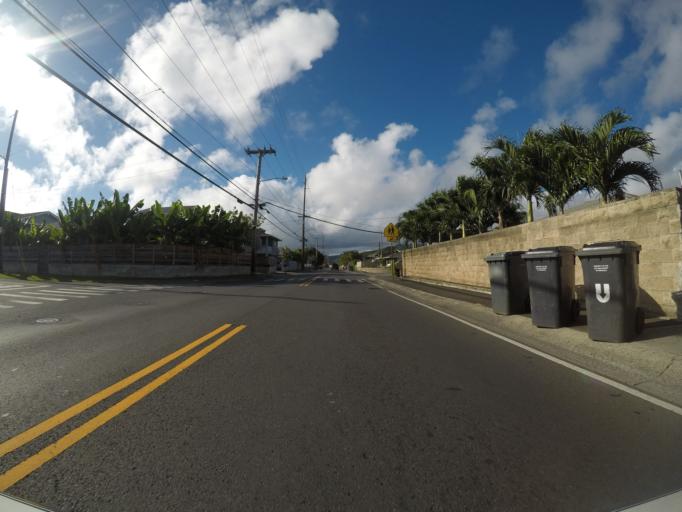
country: US
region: Hawaii
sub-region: Honolulu County
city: Kailua
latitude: 21.4000
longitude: -157.7479
